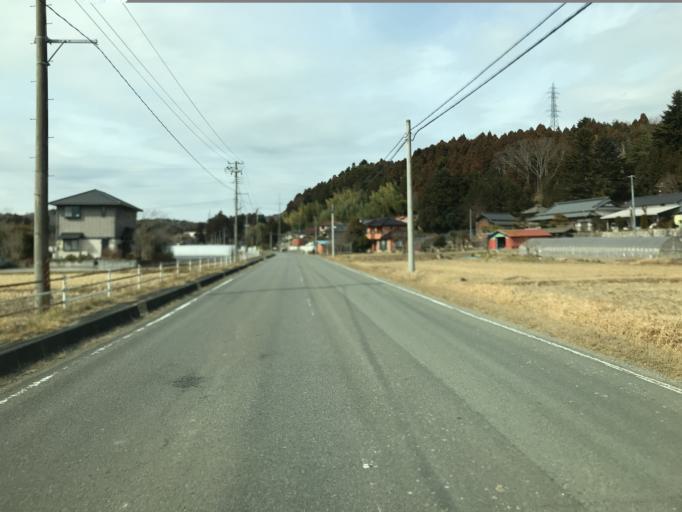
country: JP
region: Fukushima
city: Iwaki
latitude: 37.1199
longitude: 140.9417
